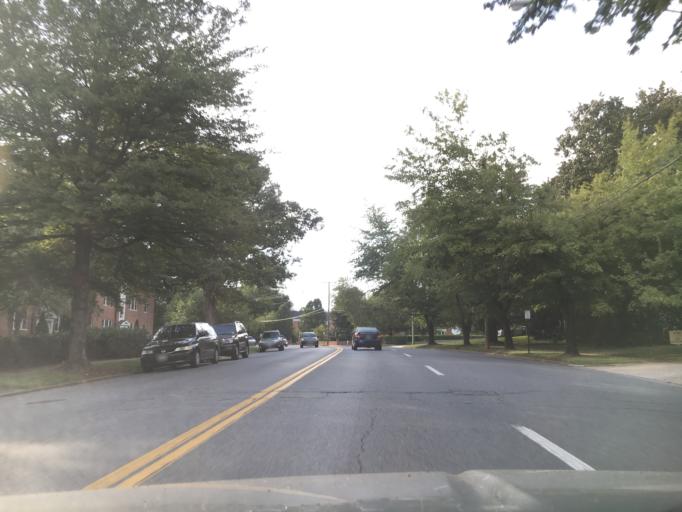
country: US
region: Virginia
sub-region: City of Lynchburg
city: West Lynchburg
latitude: 37.4382
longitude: -79.1776
